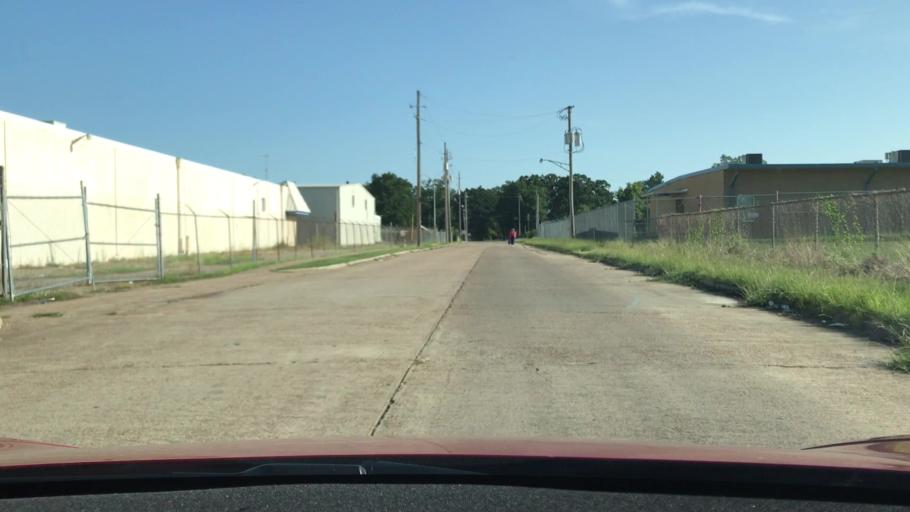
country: US
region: Louisiana
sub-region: Bossier Parish
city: Bossier City
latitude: 32.4400
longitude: -93.7652
